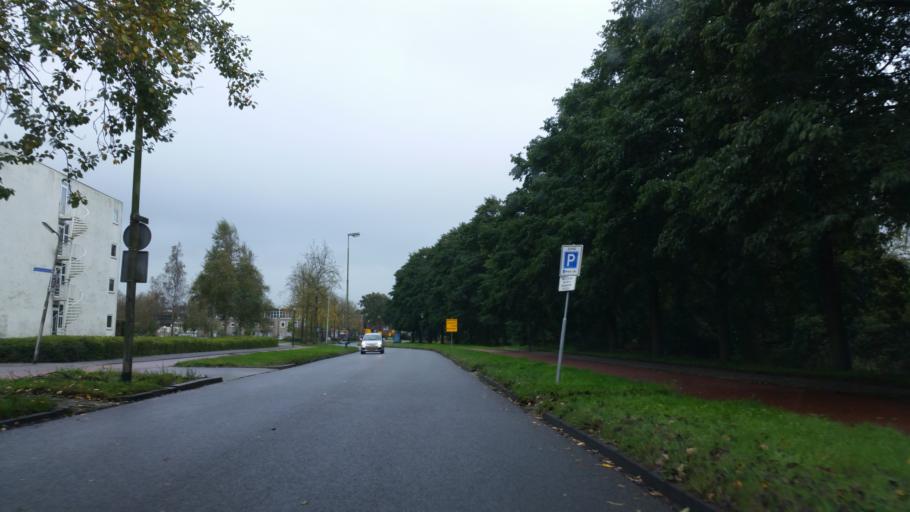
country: NL
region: Friesland
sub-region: Gemeente Leeuwarden
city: Bilgaard
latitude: 53.2094
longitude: 5.7951
